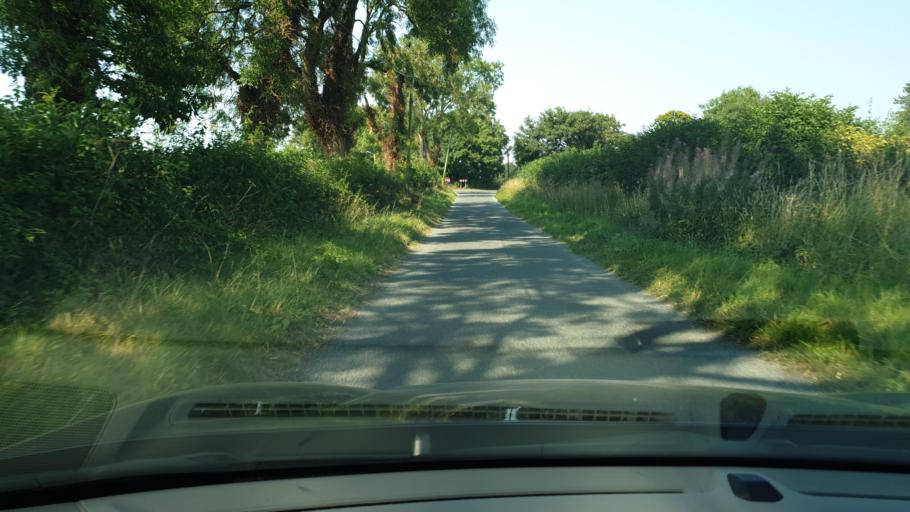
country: IE
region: Leinster
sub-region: An Mhi
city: Athboy
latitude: 53.6350
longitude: -6.9805
